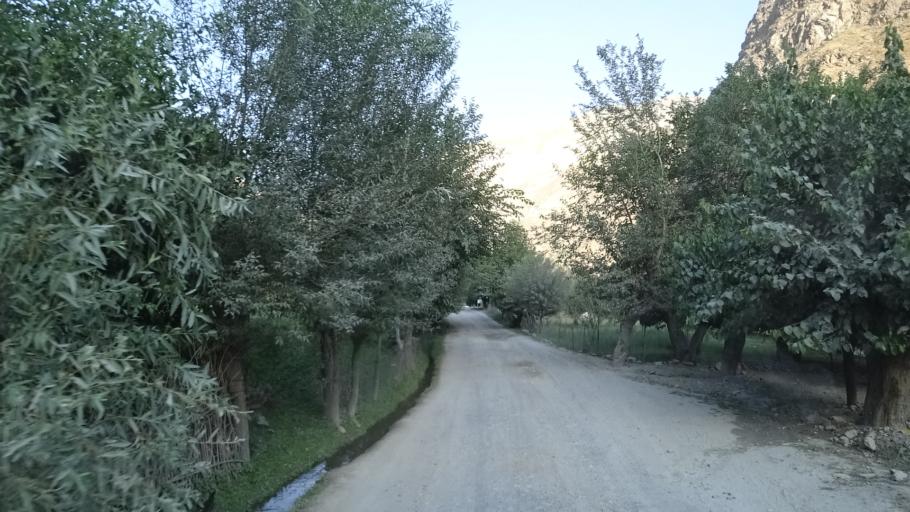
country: AF
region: Badakhshan
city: Maymay
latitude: 38.4783
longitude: 70.9576
